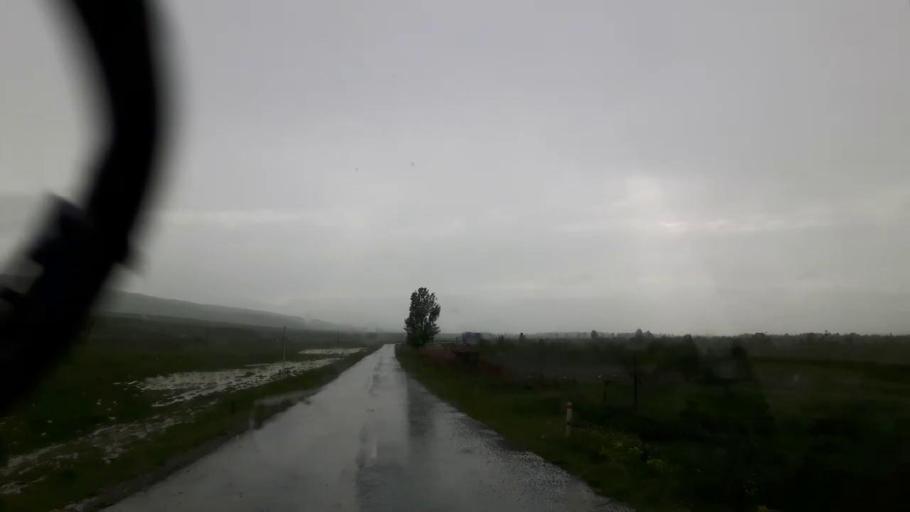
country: GE
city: Agara
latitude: 42.0145
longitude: 43.8231
